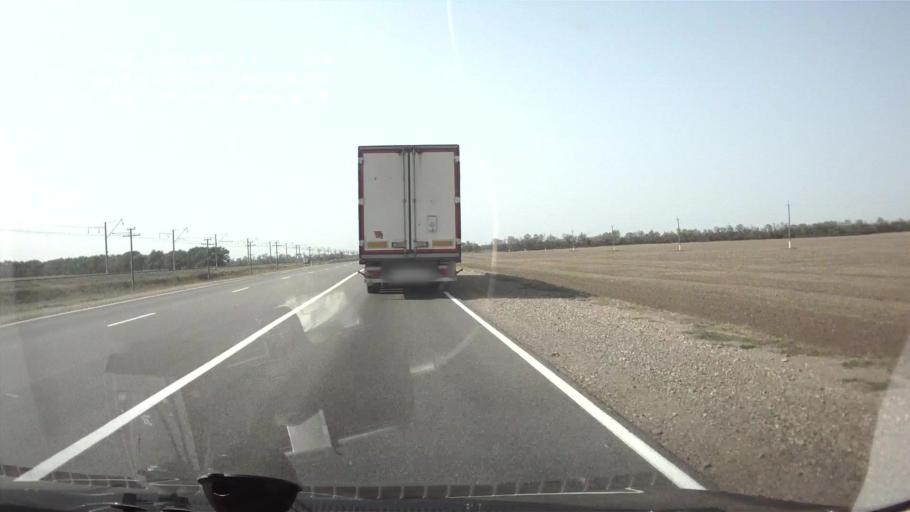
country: RU
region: Krasnodarskiy
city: Ladozhskaya
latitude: 45.3518
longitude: 40.0111
